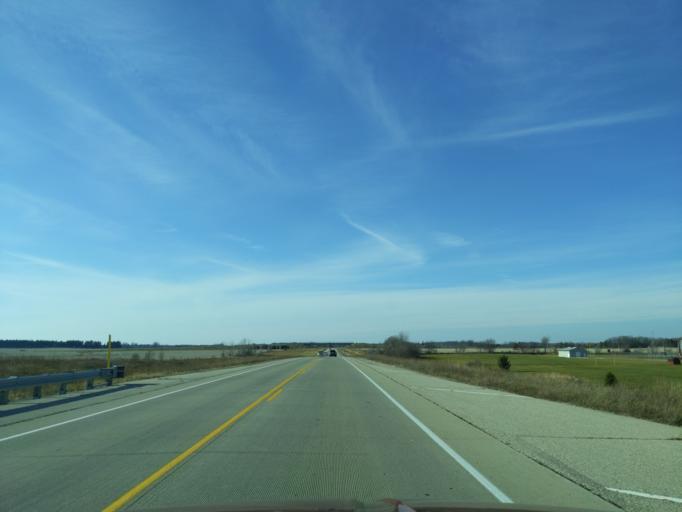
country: US
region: Wisconsin
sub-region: Walworth County
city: Whitewater
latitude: 42.8211
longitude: -88.7521
